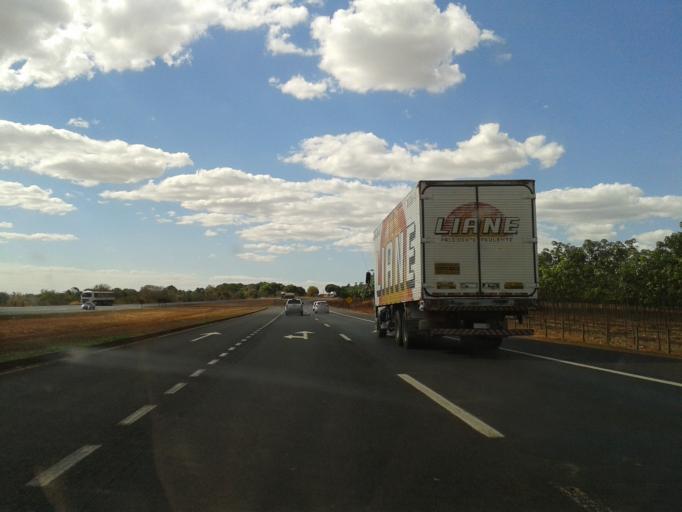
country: BR
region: Minas Gerais
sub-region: Monte Alegre De Minas
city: Monte Alegre de Minas
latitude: -18.8173
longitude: -49.0871
